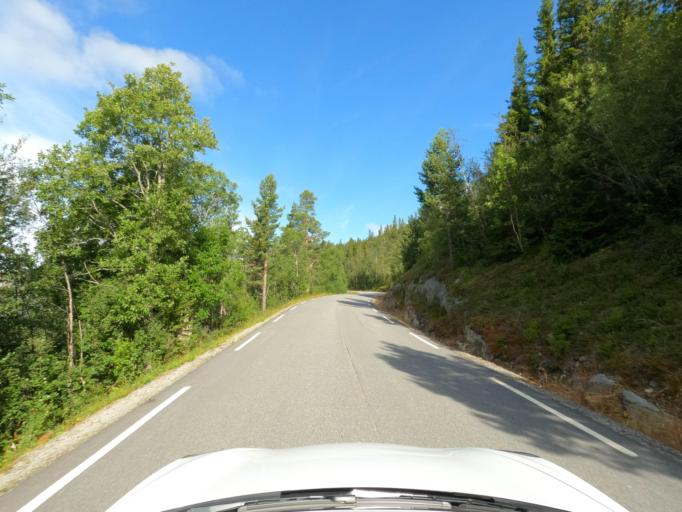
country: NO
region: Telemark
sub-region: Tinn
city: Rjukan
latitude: 60.1420
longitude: 8.6429
